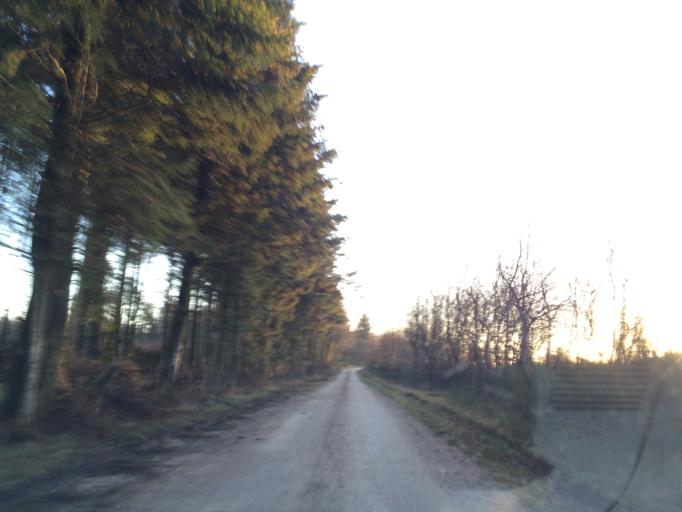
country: DK
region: Central Jutland
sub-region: Holstebro Kommune
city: Ulfborg
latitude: 56.2338
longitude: 8.4861
